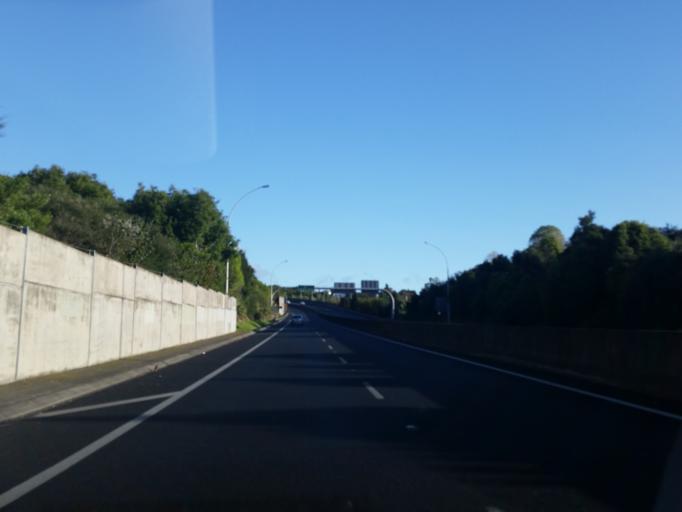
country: NZ
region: Bay of Plenty
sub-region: Tauranga City
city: Tauranga
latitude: -37.7020
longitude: 176.1387
